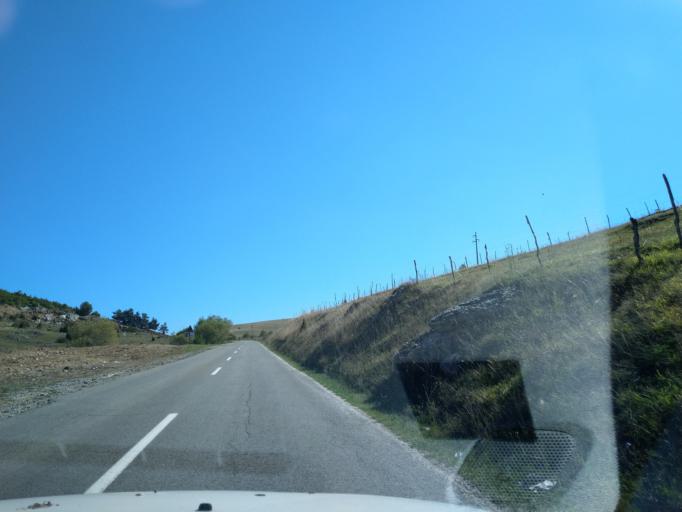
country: RS
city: Sokolovica
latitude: 43.2759
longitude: 20.1986
